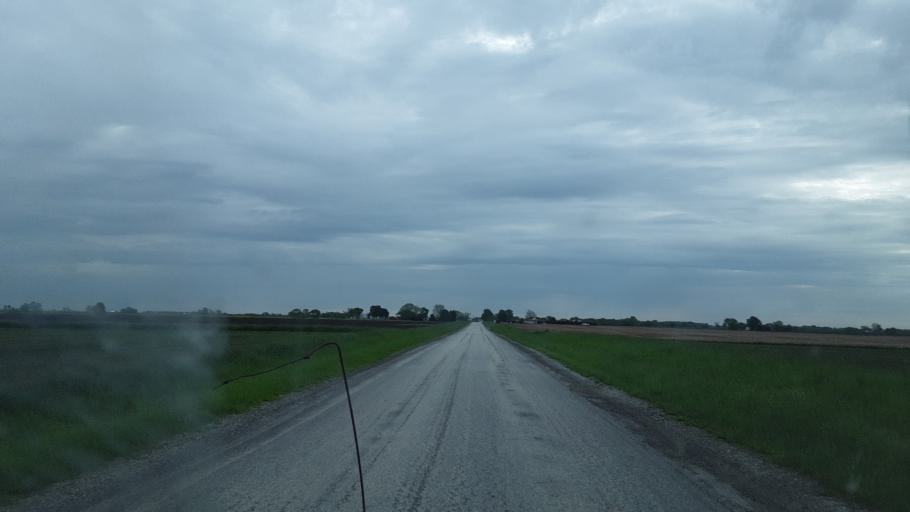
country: US
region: Illinois
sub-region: McDonough County
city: Macomb
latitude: 40.3819
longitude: -90.6683
